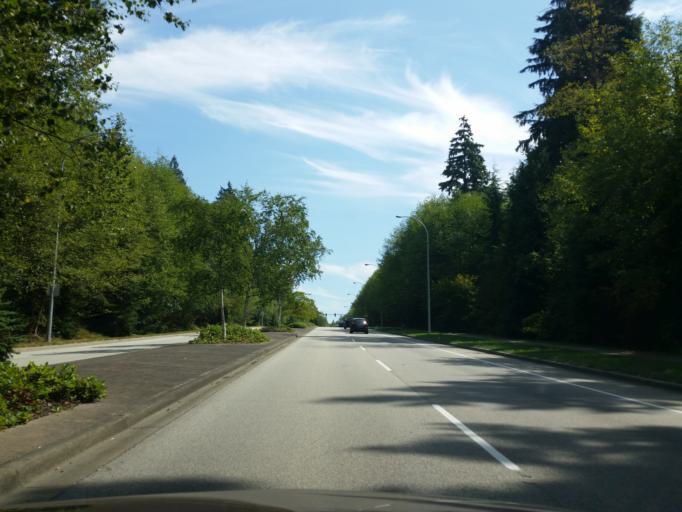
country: CA
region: British Columbia
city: Burnaby
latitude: 49.2795
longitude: -122.9493
